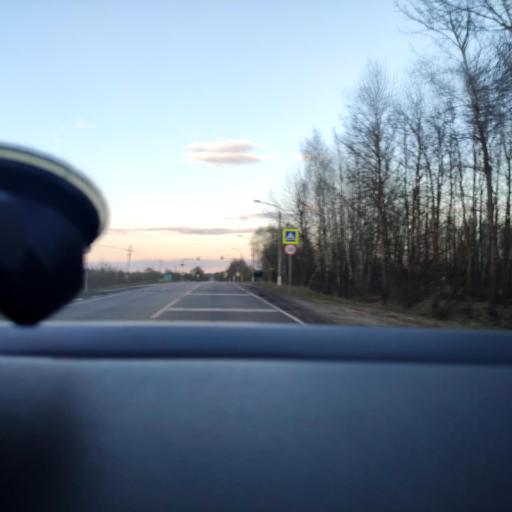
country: RU
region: Moskovskaya
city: Krasnyy Tkach
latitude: 55.4284
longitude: 39.2117
